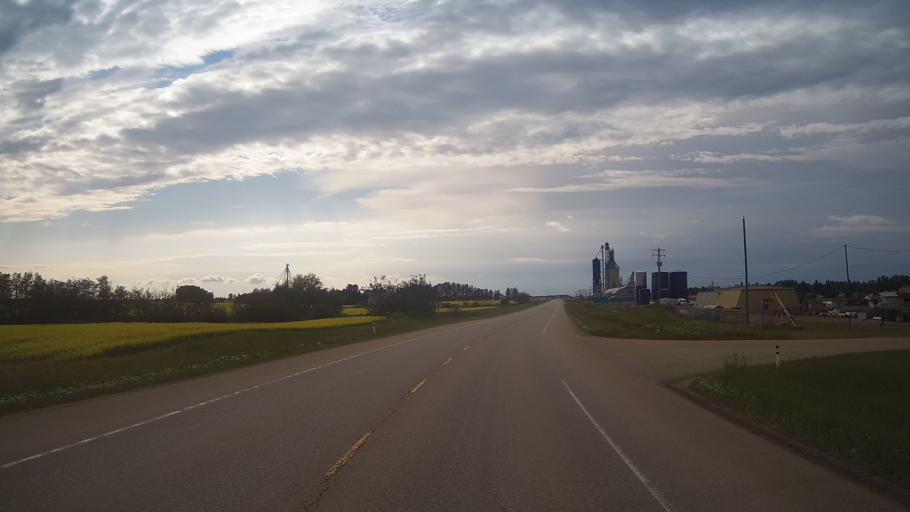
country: CA
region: Alberta
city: Viking
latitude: 53.0883
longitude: -111.7673
